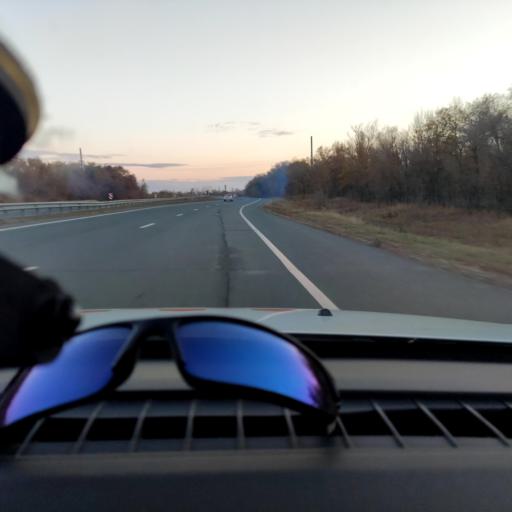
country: RU
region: Samara
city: Novokuybyshevsk
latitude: 53.0458
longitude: 50.0062
